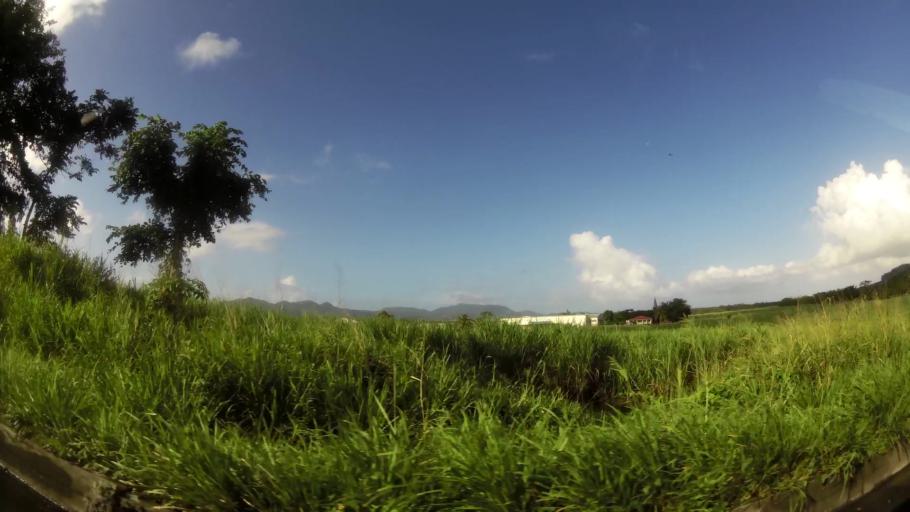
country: MQ
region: Martinique
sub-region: Martinique
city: Ducos
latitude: 14.5575
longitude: -60.9723
